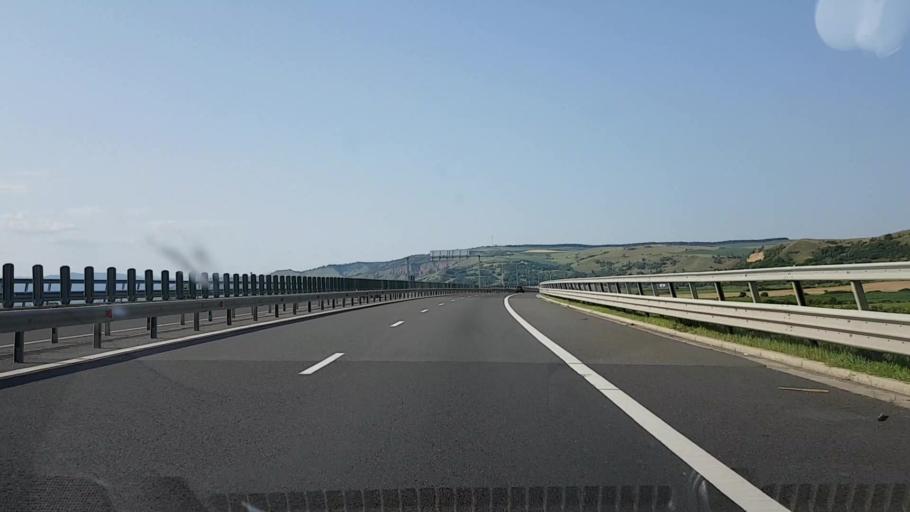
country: RO
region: Alba
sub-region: Municipiul Sebes
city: Sebes
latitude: 45.9477
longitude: 23.5931
